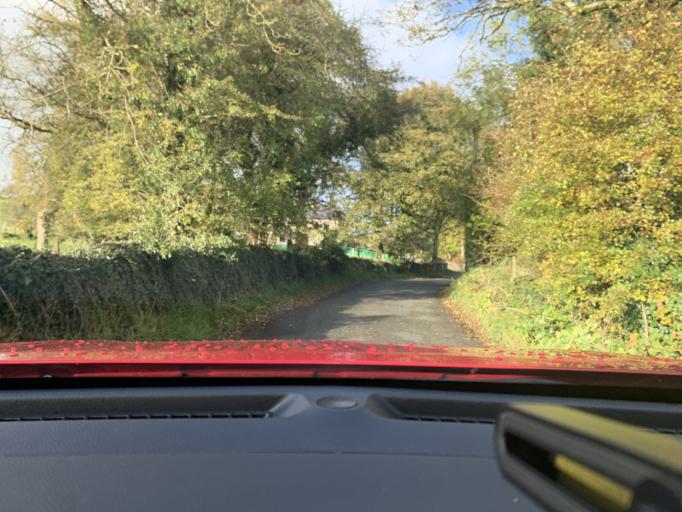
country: IE
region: Connaught
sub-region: Sligo
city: Ballymote
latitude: 54.1026
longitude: -8.4341
